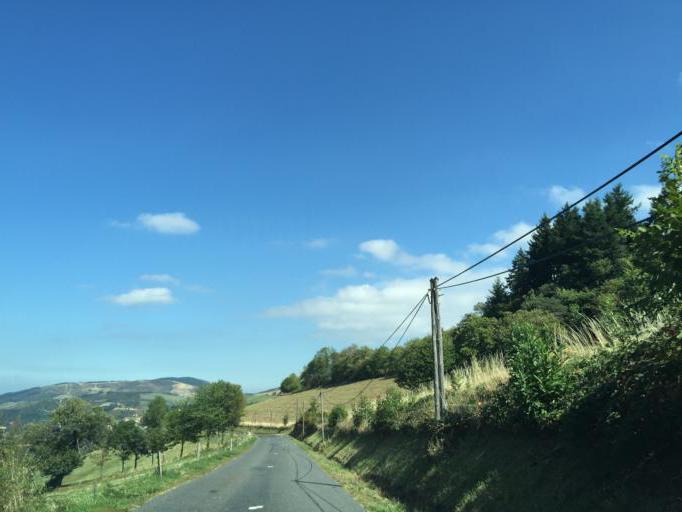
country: FR
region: Rhone-Alpes
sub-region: Departement de la Loire
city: Saint-Paul-en-Jarez
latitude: 45.4259
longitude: 4.5675
